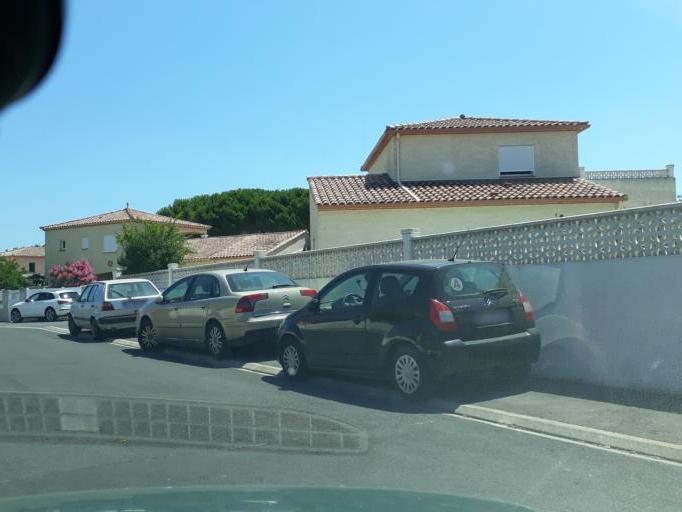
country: FR
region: Languedoc-Roussillon
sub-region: Departement de l'Herault
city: Agde
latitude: 43.2887
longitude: 3.4496
